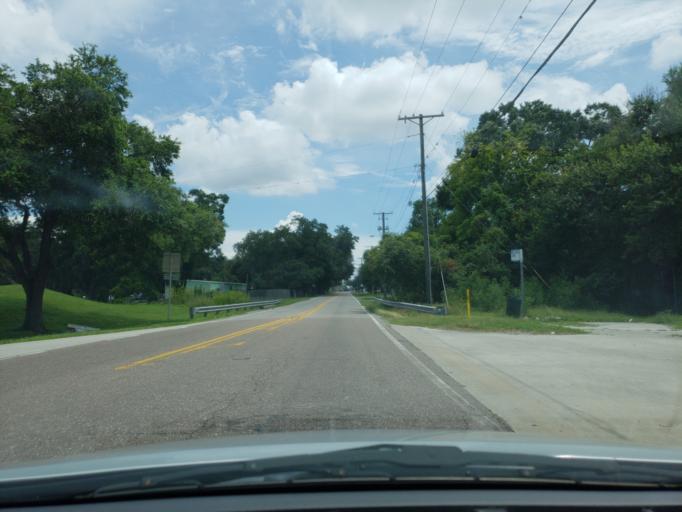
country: US
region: Florida
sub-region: Hillsborough County
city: East Lake-Orient Park
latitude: 27.9878
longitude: -82.3731
